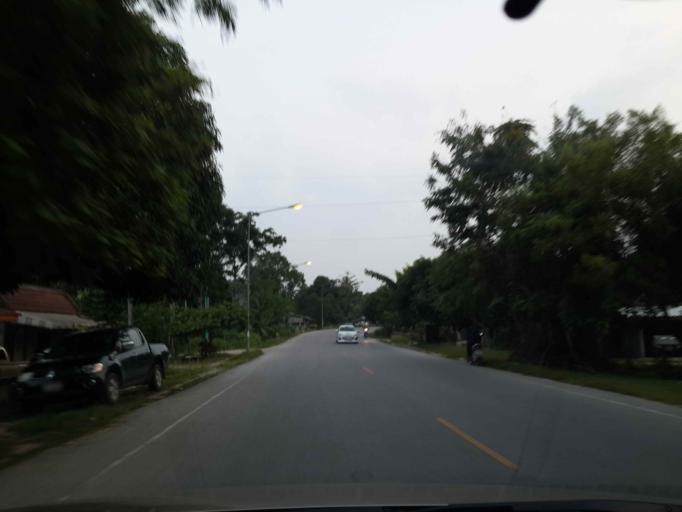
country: TH
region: Narathiwat
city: Rueso
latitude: 6.3602
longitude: 101.4677
